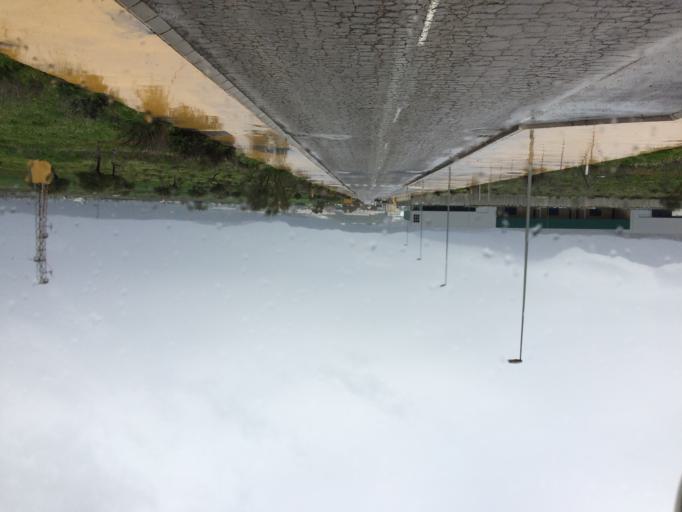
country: ES
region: Andalusia
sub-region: Provincia de Malaga
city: Antequera
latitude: 37.0465
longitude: -4.5196
